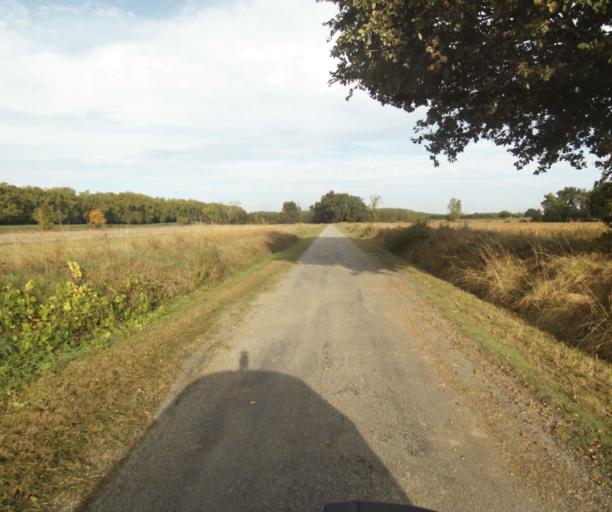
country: FR
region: Midi-Pyrenees
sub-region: Departement du Tarn-et-Garonne
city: Montech
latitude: 43.9749
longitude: 1.2249
